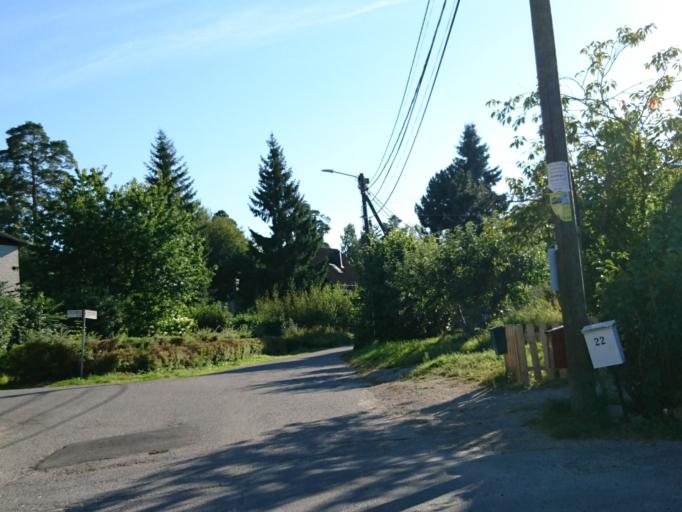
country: SE
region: Stockholm
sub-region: Huddinge Kommun
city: Segeltorp
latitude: 59.2769
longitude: 17.9390
